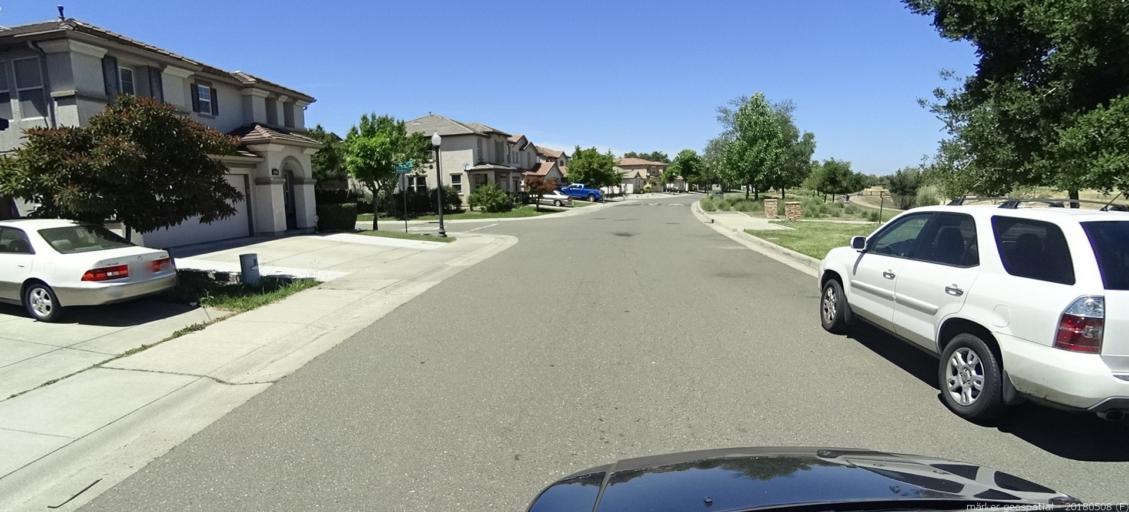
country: US
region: California
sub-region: Sacramento County
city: Elverta
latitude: 38.6629
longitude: -121.5252
